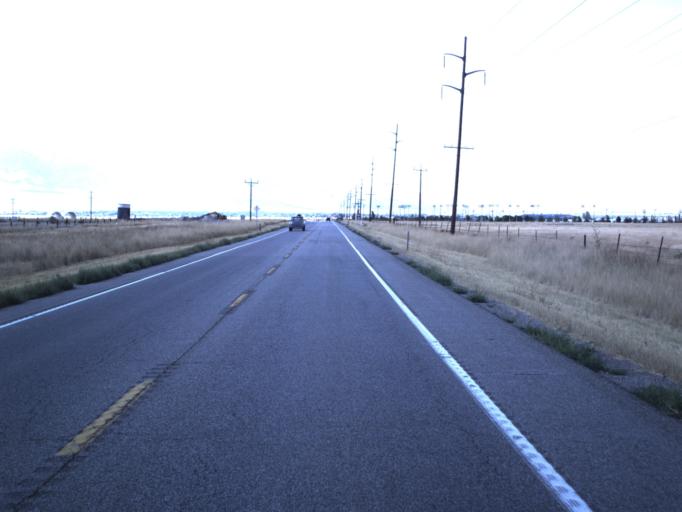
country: US
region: Utah
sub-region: Tooele County
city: Tooele
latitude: 40.5641
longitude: -112.3609
